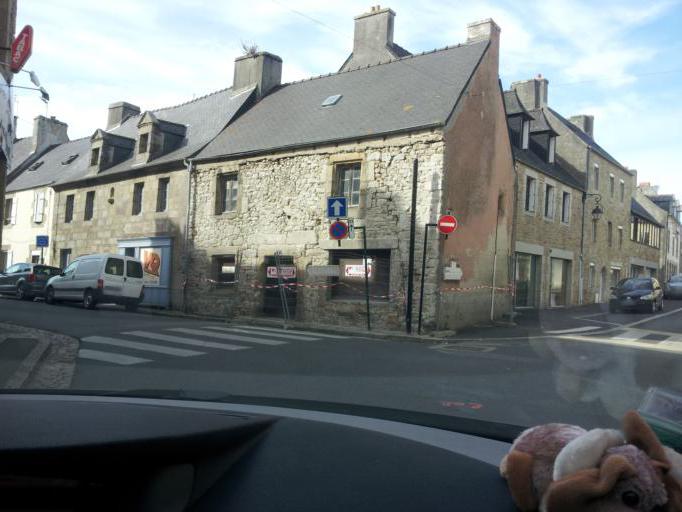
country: FR
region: Brittany
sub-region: Departement du Finistere
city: Saint-Pol-de-Leon
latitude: 48.6852
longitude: -3.9885
